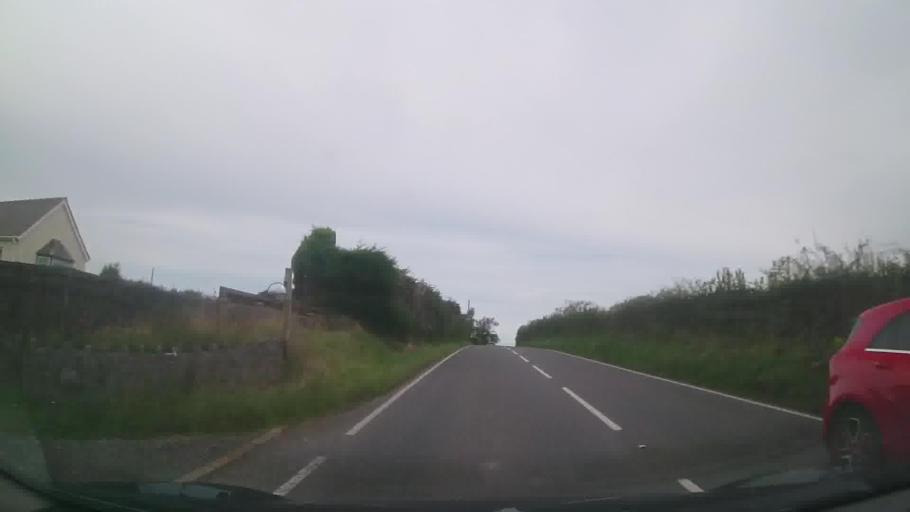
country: GB
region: Wales
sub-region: Pembrokeshire
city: Kilgetty
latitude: 51.7471
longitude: -4.7307
